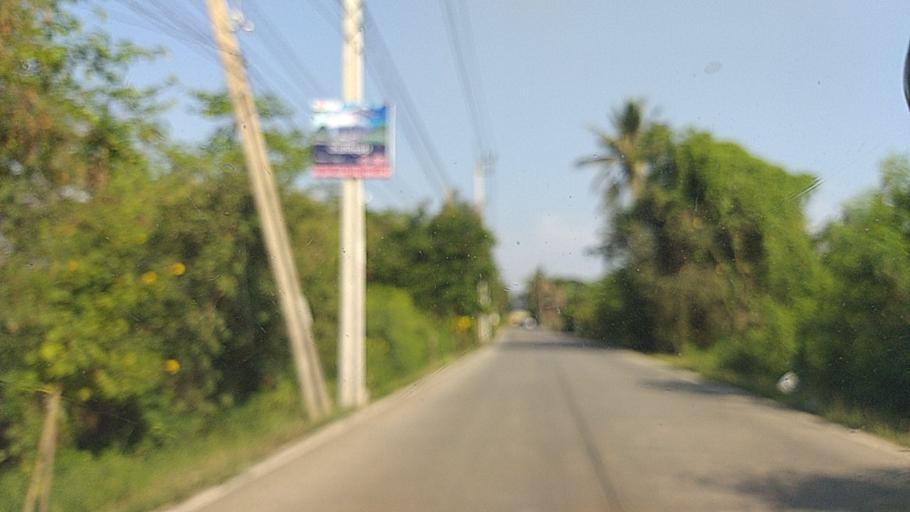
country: TH
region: Nonthaburi
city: Sai Noi
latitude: 13.9355
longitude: 100.3419
